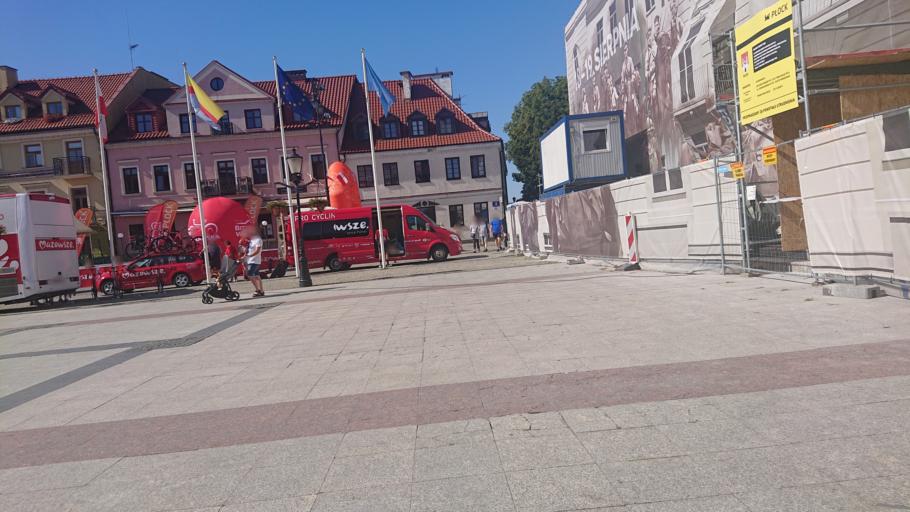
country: PL
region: Masovian Voivodeship
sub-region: Plock
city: Plock
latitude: 52.5453
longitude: 19.6849
